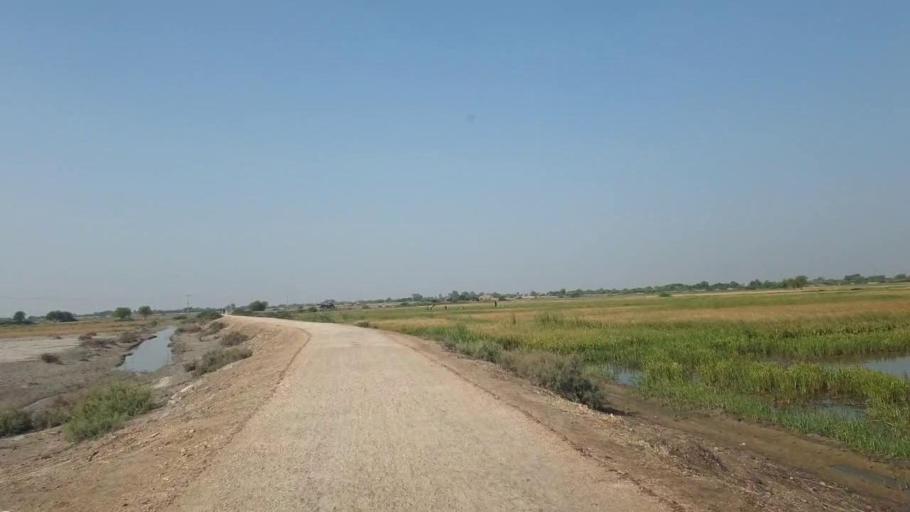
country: PK
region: Sindh
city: Badin
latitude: 24.5214
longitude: 68.7718
